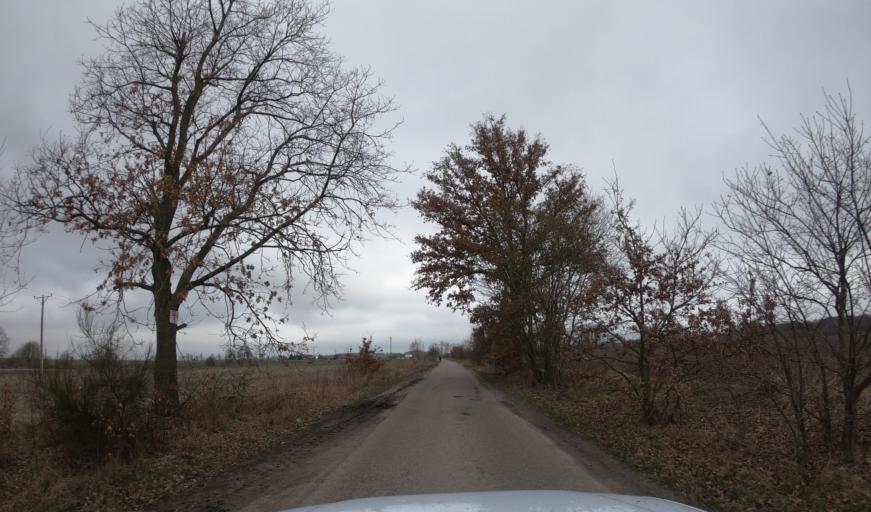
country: PL
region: West Pomeranian Voivodeship
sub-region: Powiat gryficki
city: Cerkwica
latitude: 53.9959
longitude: 15.1043
